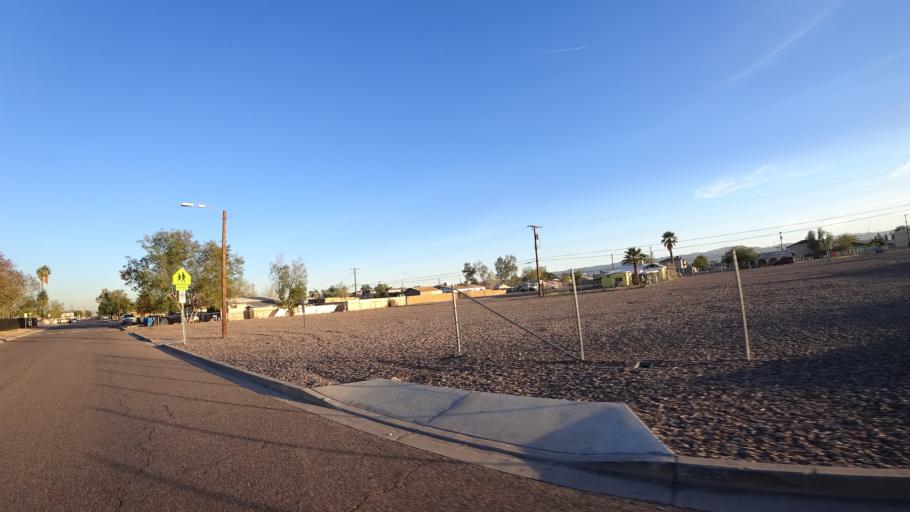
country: US
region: Arizona
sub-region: Maricopa County
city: Phoenix
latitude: 33.4332
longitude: -112.0600
